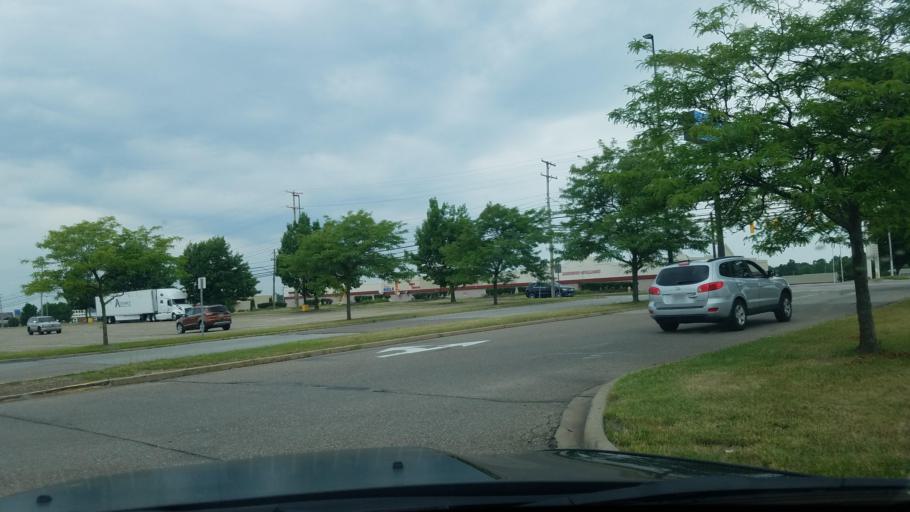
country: US
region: Ohio
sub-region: Mahoning County
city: Austintown
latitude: 41.0991
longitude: -80.7732
